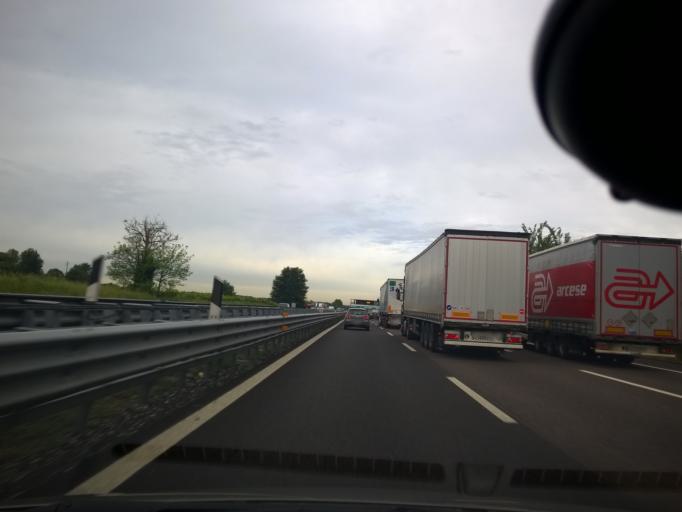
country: IT
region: Veneto
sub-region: Provincia di Verona
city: Cavalcaselle
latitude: 45.4295
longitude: 10.7236
